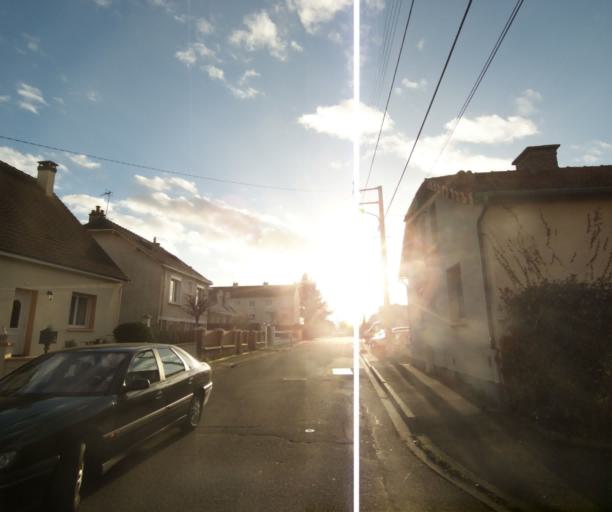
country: FR
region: Pays de la Loire
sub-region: Departement de la Sarthe
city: Allonnes
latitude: 47.9896
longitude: 0.1722
